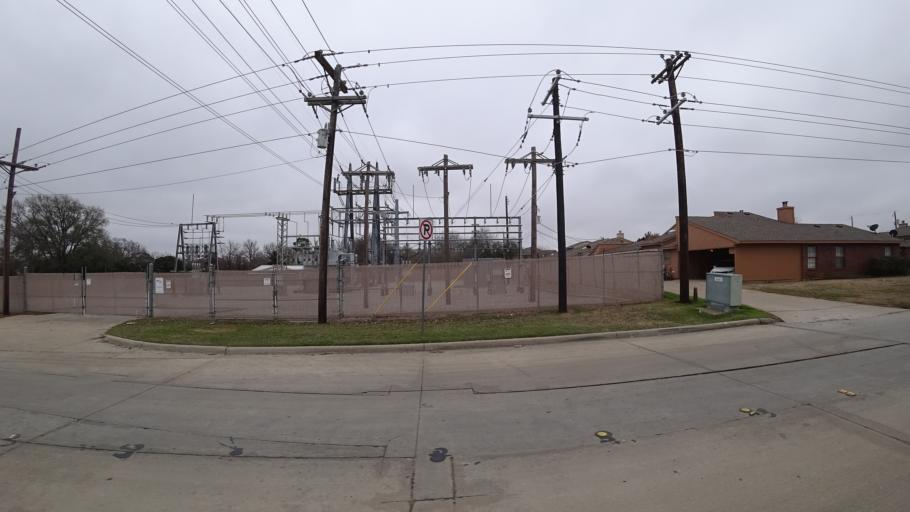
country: US
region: Texas
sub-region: Denton County
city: Lewisville
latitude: 33.0641
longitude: -97.0097
